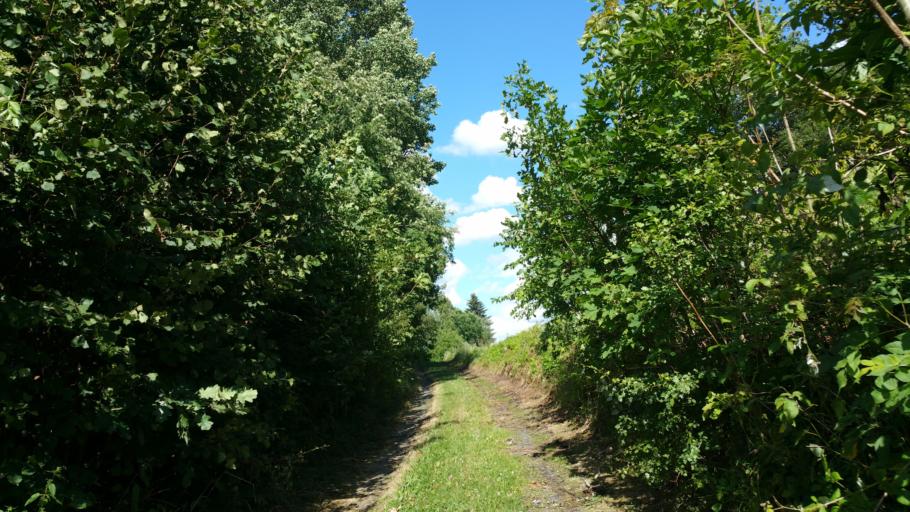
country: DE
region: Bavaria
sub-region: Upper Franconia
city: Schwarzenbach an der Saale
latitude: 50.2142
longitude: 11.9240
